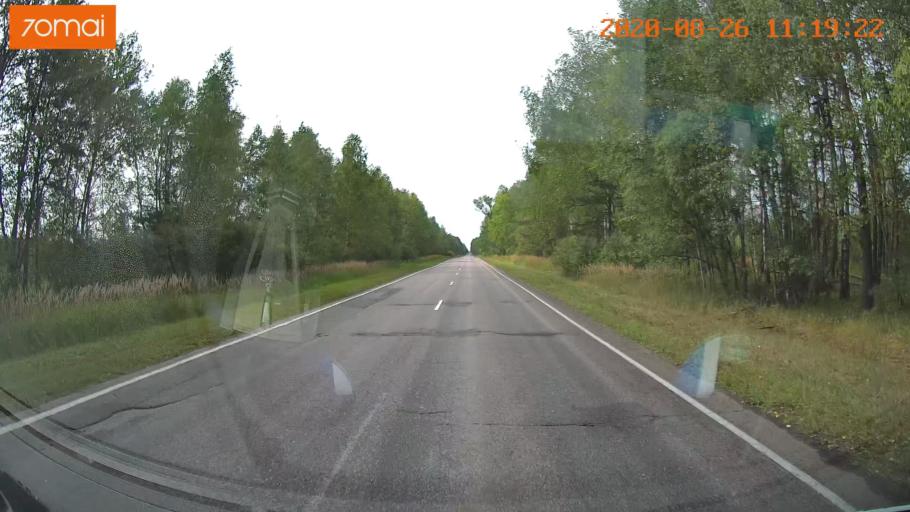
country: RU
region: Rjazan
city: Shilovo
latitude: 54.3999
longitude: 41.0809
